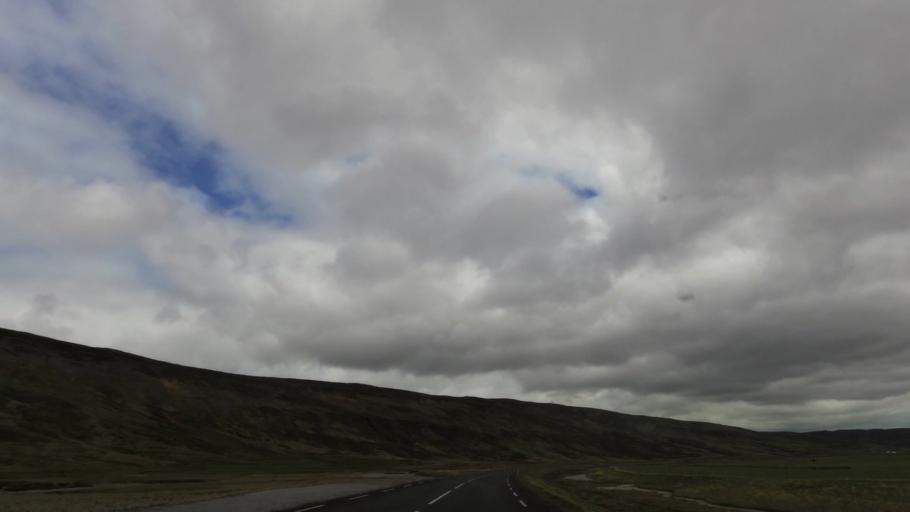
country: IS
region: West
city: Stykkisholmur
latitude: 65.7639
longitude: -21.8378
